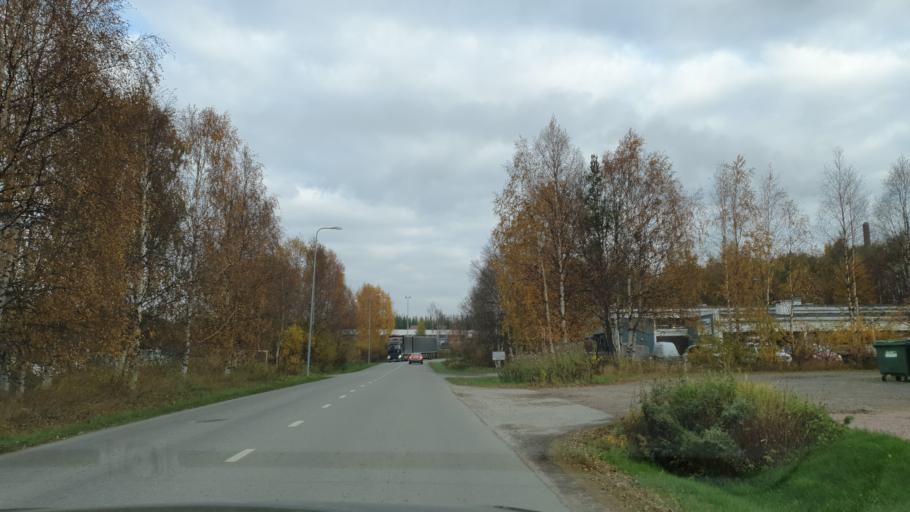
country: FI
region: Lapland
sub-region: Rovaniemi
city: Rovaniemi
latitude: 66.4935
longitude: 25.6652
